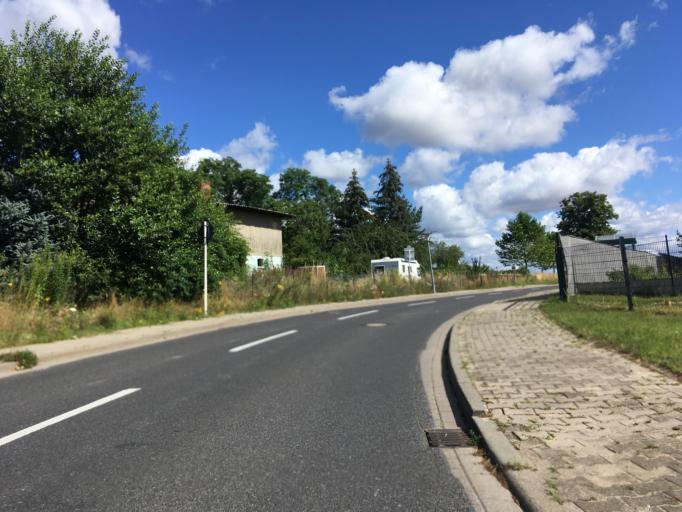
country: DE
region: Brandenburg
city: Templin
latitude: 53.1709
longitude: 13.5617
